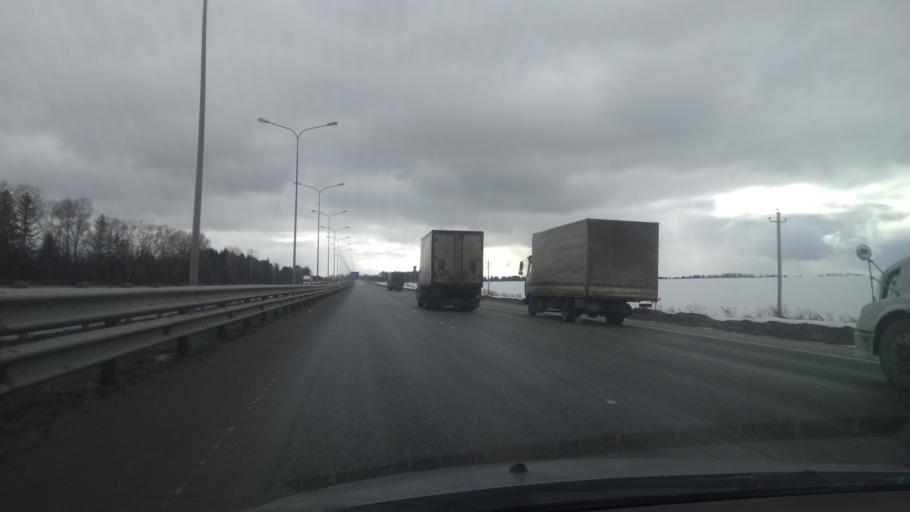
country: RU
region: Perm
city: Bershet'
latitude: 57.6900
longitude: 56.4039
